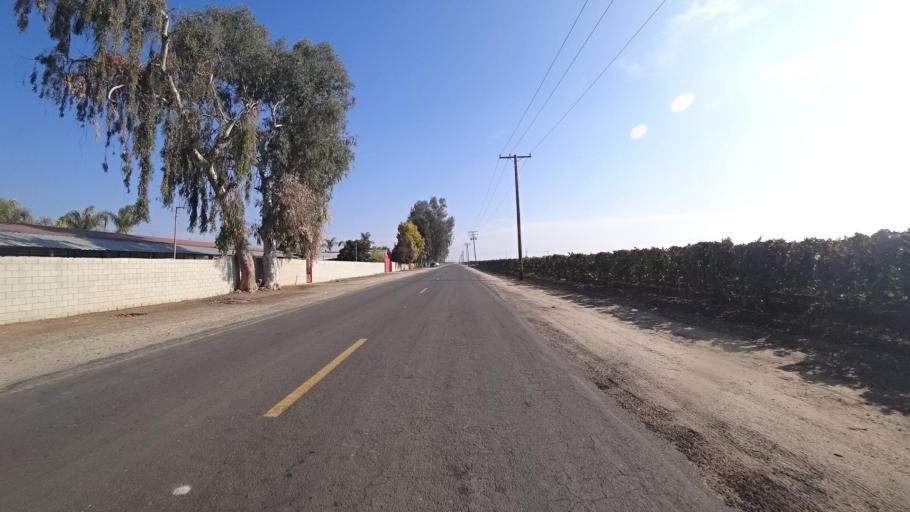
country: US
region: California
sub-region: Kern County
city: McFarland
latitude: 35.6892
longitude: -119.1915
